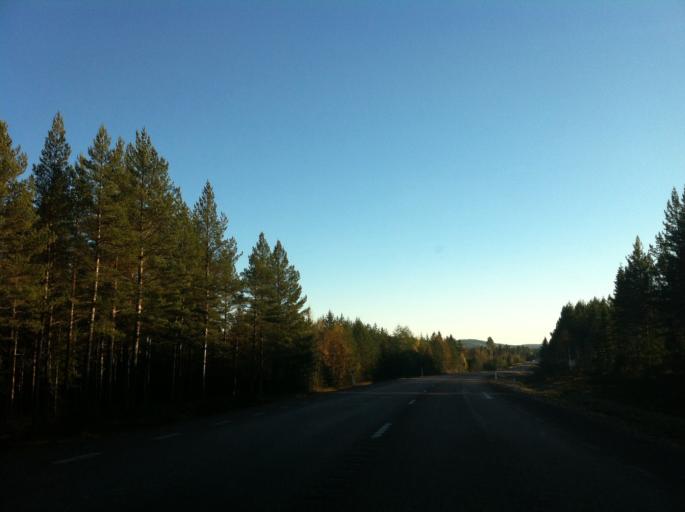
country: SE
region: Dalarna
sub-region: Rattviks Kommun
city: Raettvik
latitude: 60.8234
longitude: 15.2524
